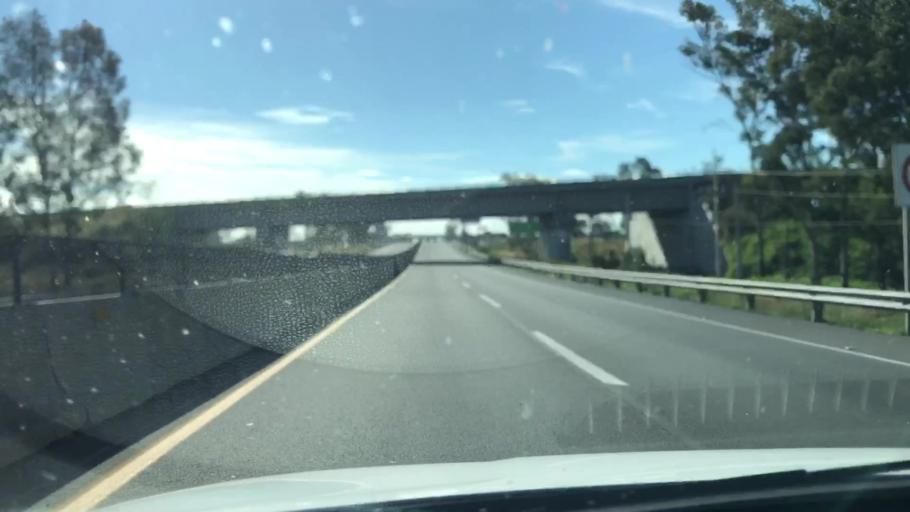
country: MX
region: Guanajuato
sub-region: Leon
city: Centro Familiar la Soledad
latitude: 21.0996
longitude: -101.7803
